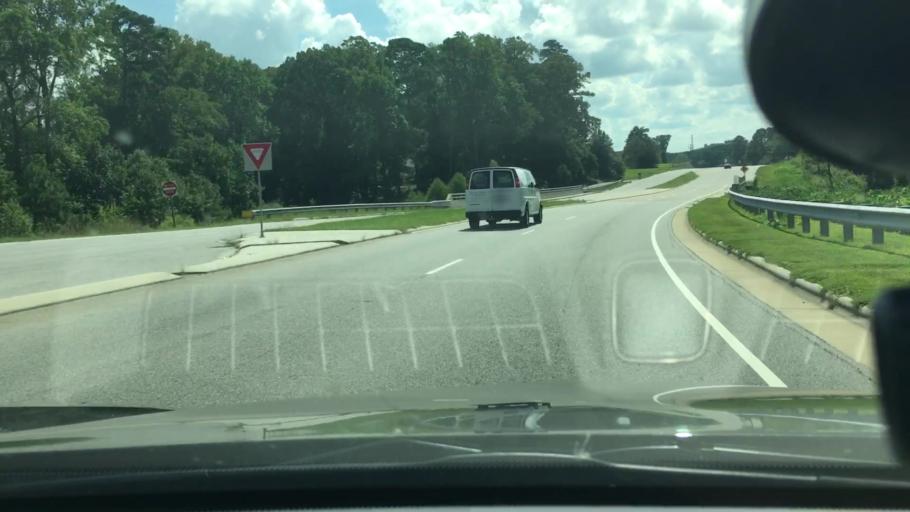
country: US
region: North Carolina
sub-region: Pitt County
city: Greenville
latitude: 35.6238
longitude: -77.4201
